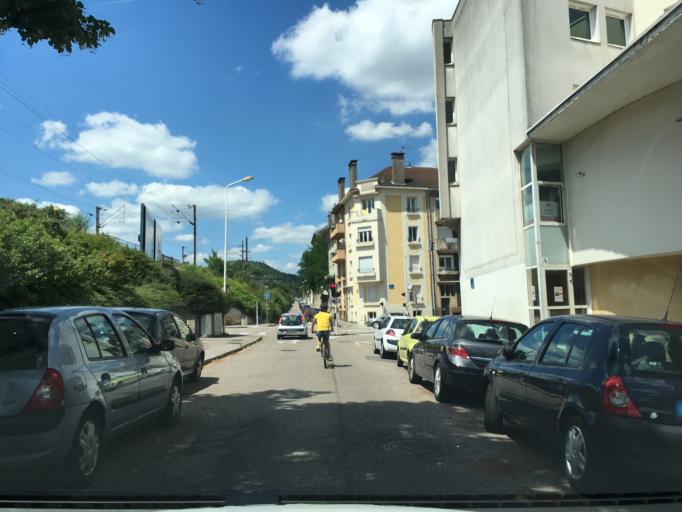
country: FR
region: Lorraine
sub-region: Departement de Meurthe-et-Moselle
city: Maxeville
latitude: 48.7003
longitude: 6.1692
